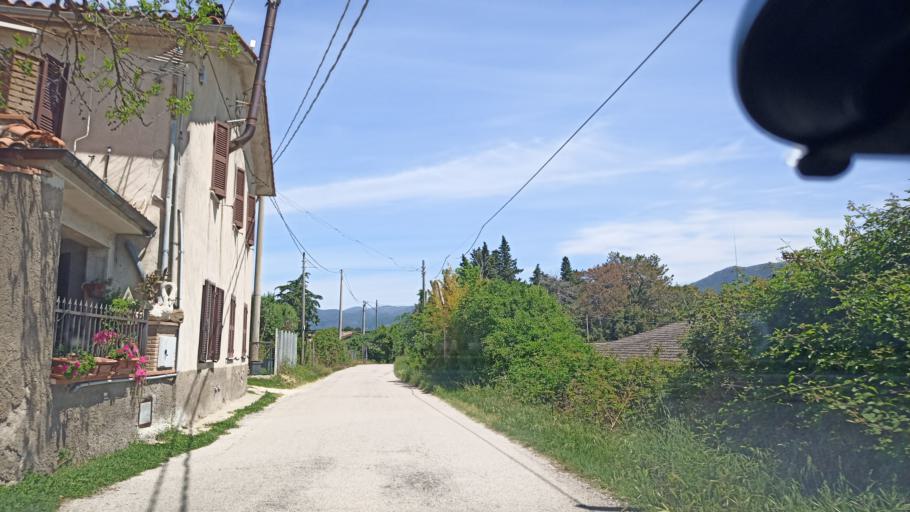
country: IT
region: Latium
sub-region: Provincia di Rieti
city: Torri in Sabina
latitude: 42.3530
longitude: 12.6310
